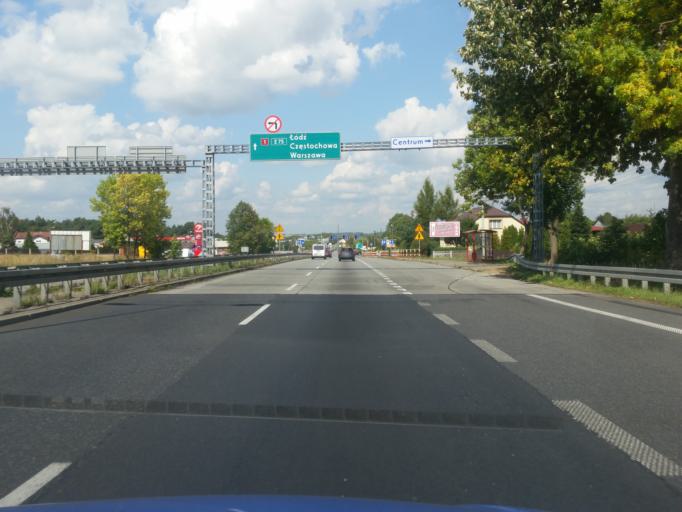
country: PL
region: Silesian Voivodeship
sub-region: Powiat bedzinski
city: Siewierz
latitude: 50.4641
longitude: 19.2309
